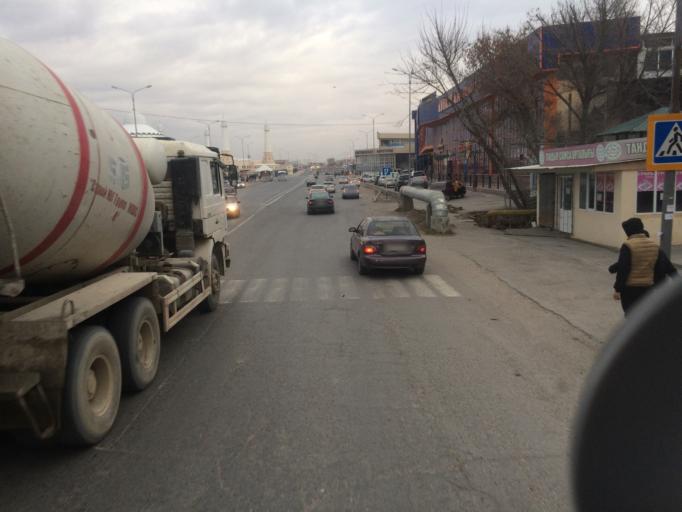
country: KZ
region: Ongtustik Qazaqstan
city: Shymkent
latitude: 42.3486
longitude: 69.5282
